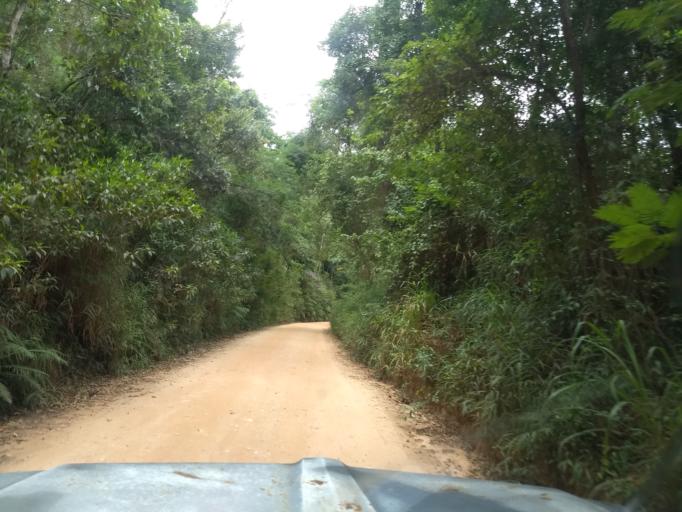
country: BR
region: Sao Paulo
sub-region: Cabreuva
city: Cabreuva
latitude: -23.4093
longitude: -47.2005
